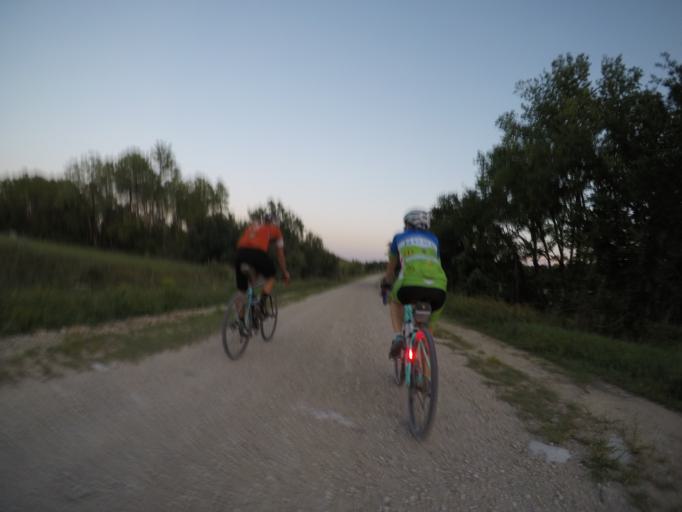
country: US
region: Kansas
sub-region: Riley County
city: Ogden
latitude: 38.9895
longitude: -96.5621
